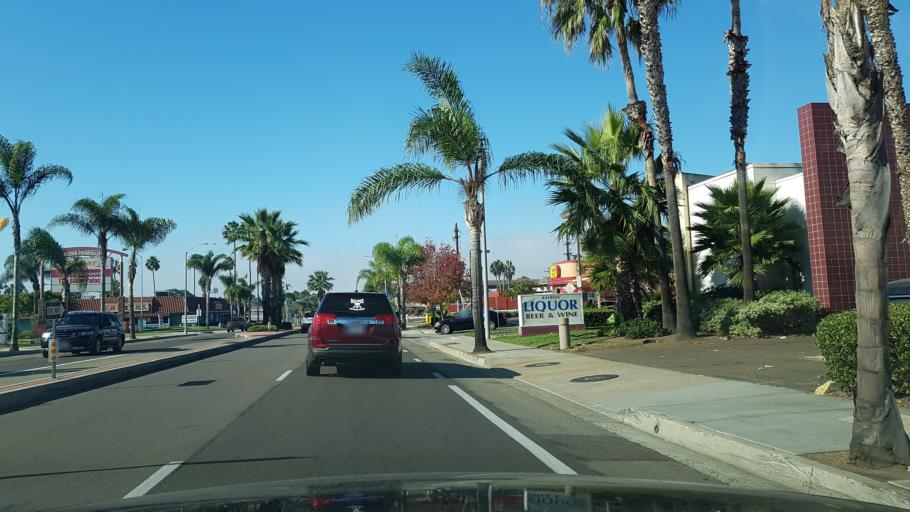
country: US
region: California
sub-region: San Diego County
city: Oceanside
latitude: 33.2028
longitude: -117.3674
